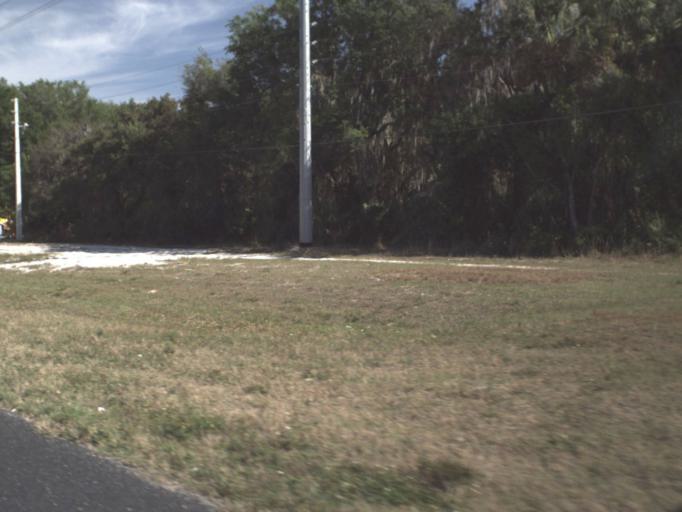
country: US
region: Florida
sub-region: Lake County
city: Hawthorne
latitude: 28.7708
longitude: -81.8845
